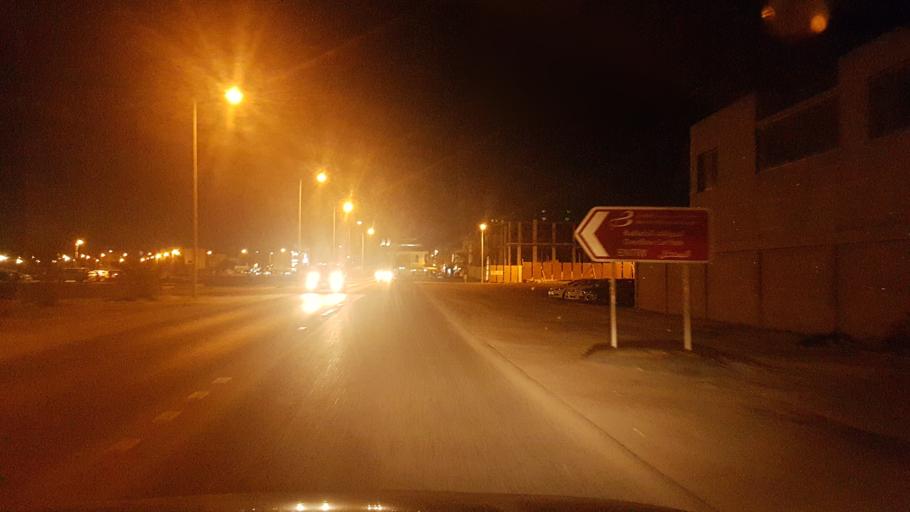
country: BH
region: Muharraq
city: Al Hadd
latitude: 26.2654
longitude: 50.6540
